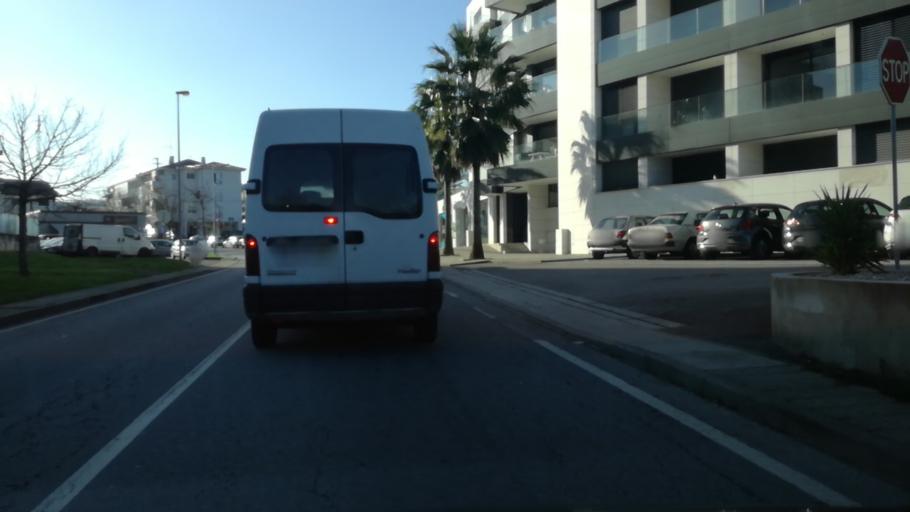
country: PT
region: Braga
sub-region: Guimaraes
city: Ponte
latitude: 41.4882
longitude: -8.3495
